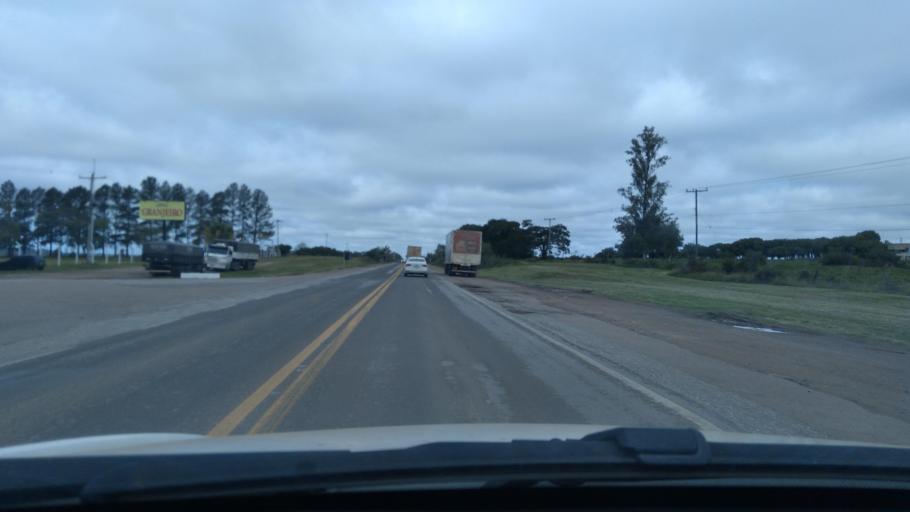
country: BR
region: Rio Grande do Sul
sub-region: Dom Pedrito
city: Dom Pedrito
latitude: -30.9776
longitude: -54.6454
